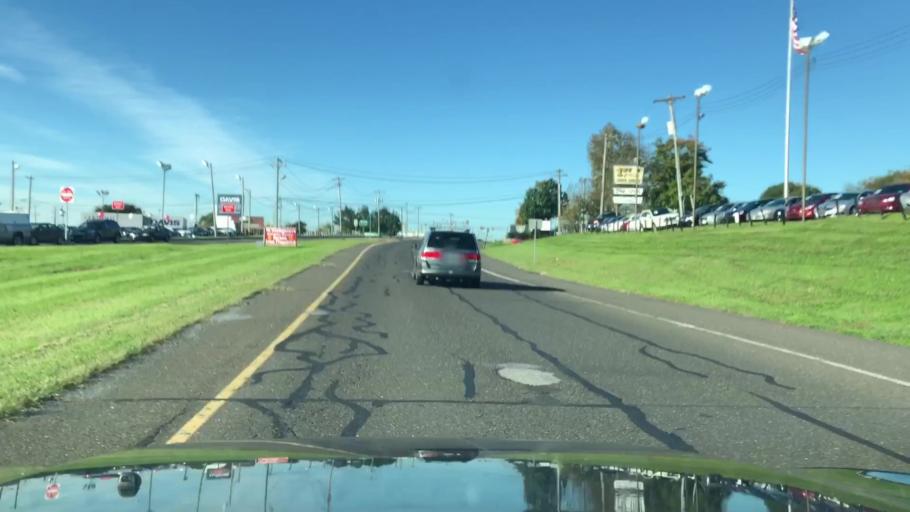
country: US
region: Pennsylvania
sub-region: Bucks County
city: Woodbourne
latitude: 40.1787
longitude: -74.8817
